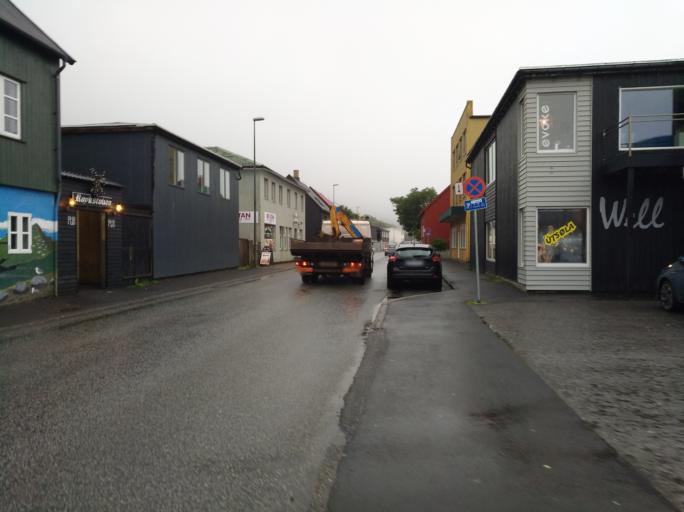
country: FO
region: Nordoyar
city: Klaksvik
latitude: 62.2276
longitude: -6.5915
